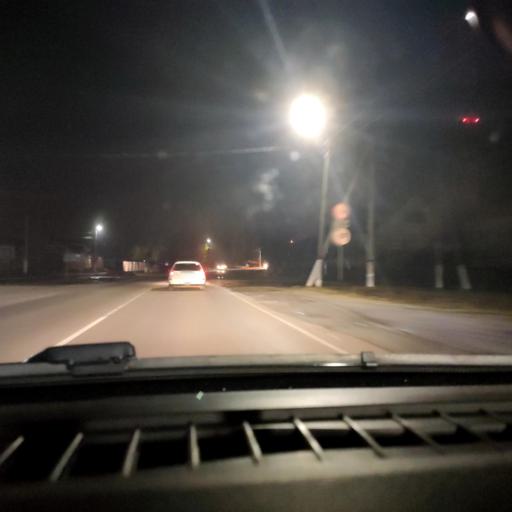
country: RU
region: Voronezj
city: Novaya Usman'
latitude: 51.6375
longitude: 39.4050
